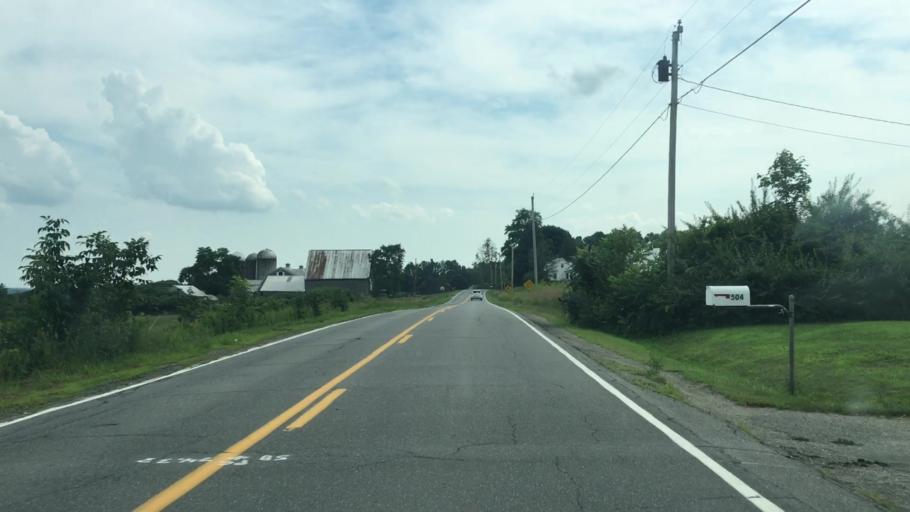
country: US
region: Maine
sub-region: Kennebec County
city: China
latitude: 44.4204
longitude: -69.5882
